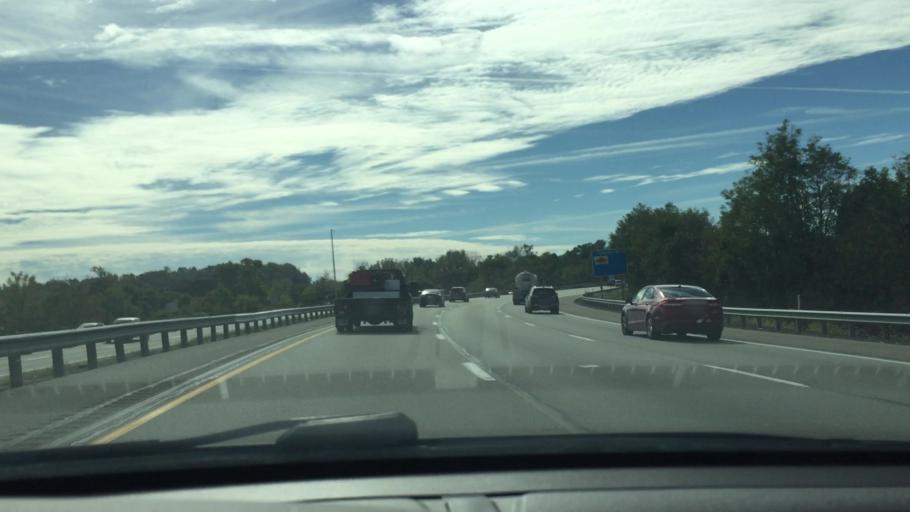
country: US
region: Pennsylvania
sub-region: Allegheny County
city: Heidelberg
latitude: 40.3830
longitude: -80.0966
